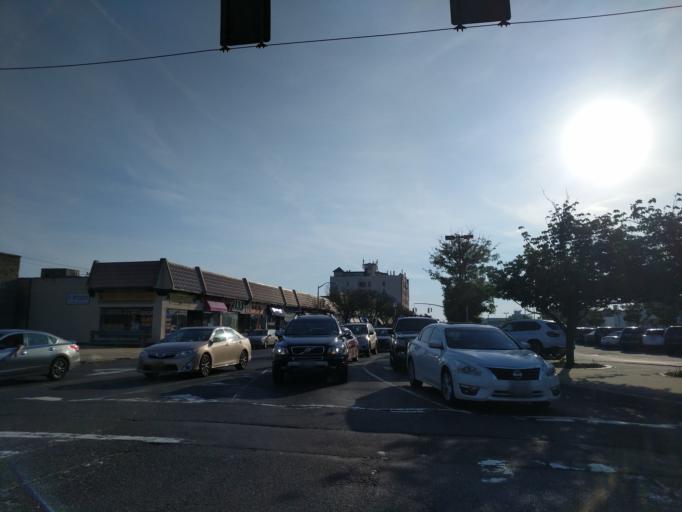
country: US
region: New York
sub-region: Nassau County
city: Long Beach
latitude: 40.5886
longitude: -73.6583
